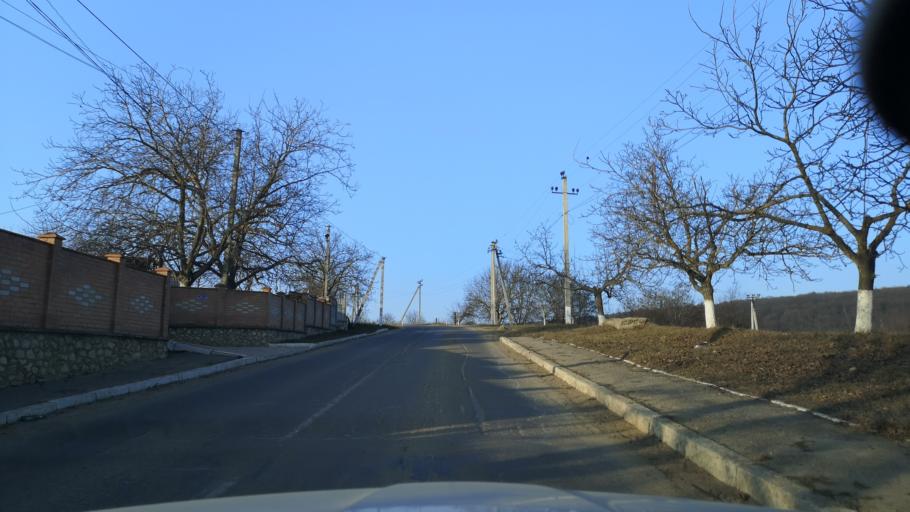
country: MD
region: Stinga Nistrului
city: Bucovat
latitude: 47.1225
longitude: 28.5036
